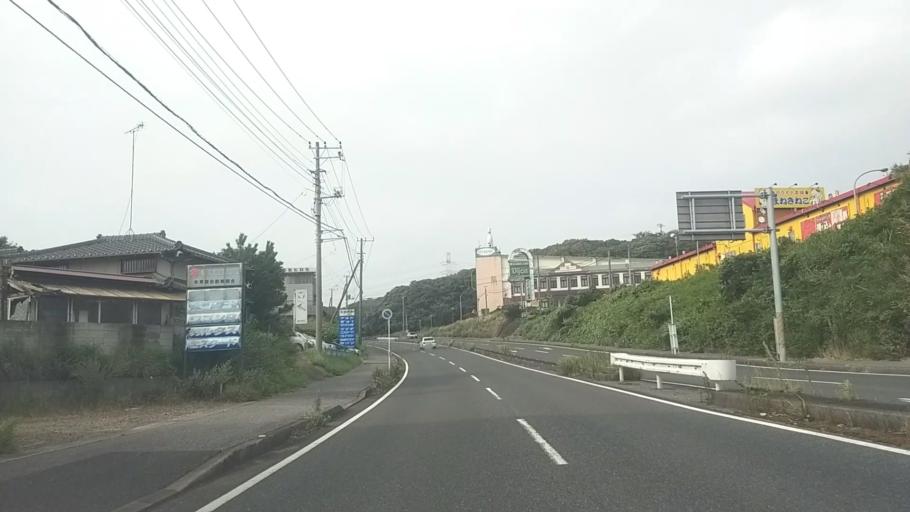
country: JP
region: Chiba
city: Kimitsu
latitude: 35.3383
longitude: 139.8913
